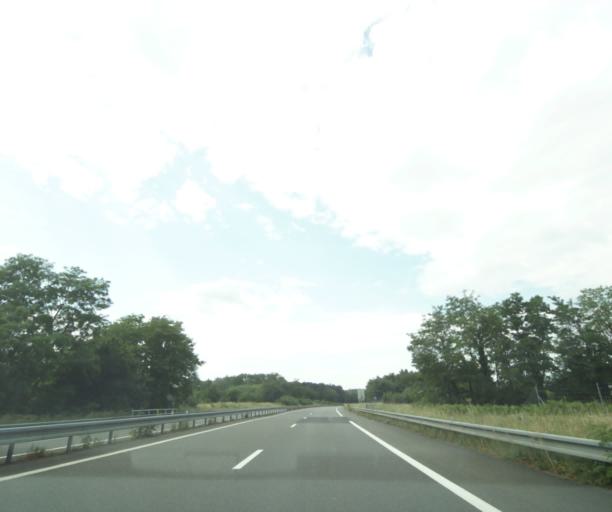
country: FR
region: Pays de la Loire
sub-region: Departement de Maine-et-Loire
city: Brion
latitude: 47.4346
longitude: -0.1673
